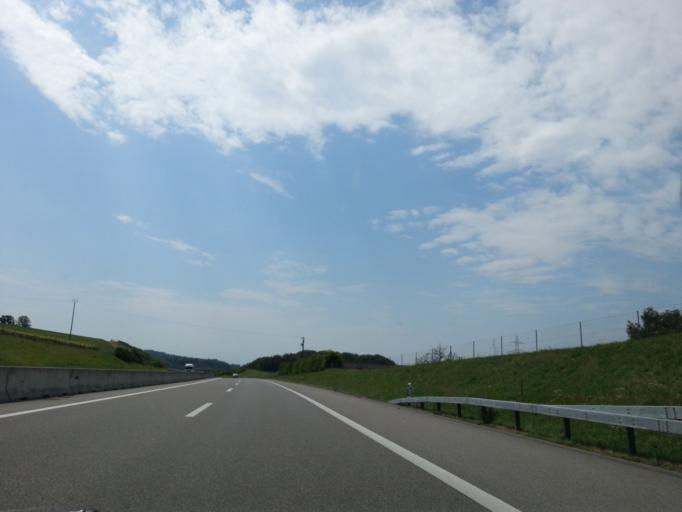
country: CH
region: Fribourg
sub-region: See District
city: Kerzers
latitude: 46.9581
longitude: 7.1714
